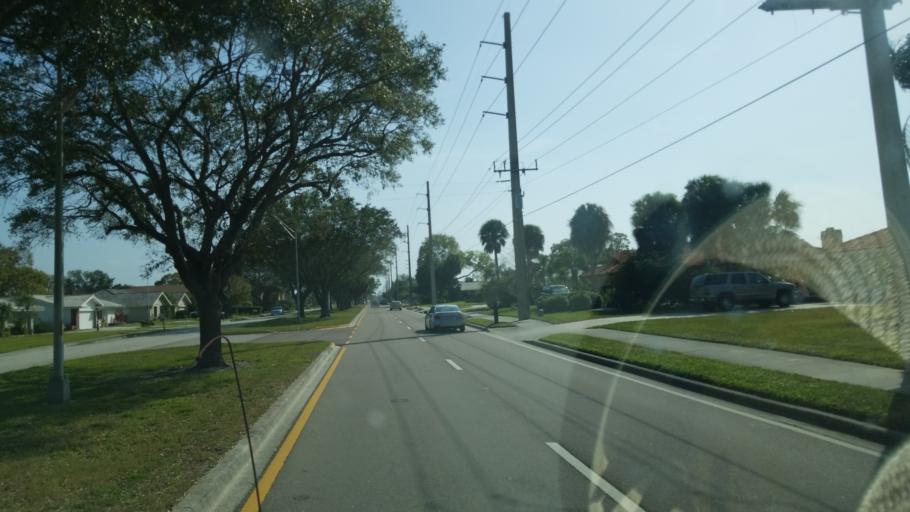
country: US
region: Florida
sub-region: Sarasota County
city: Southgate
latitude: 27.3152
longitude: -82.4965
